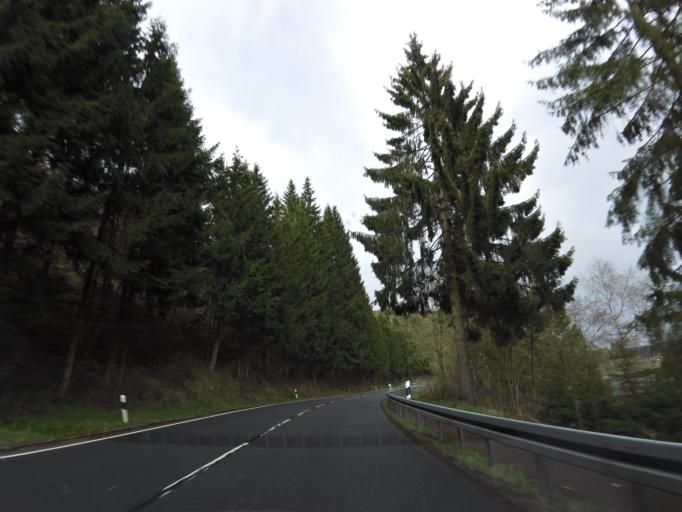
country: DE
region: Lower Saxony
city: Schulenberg im Oberharz
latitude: 51.8461
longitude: 10.4518
